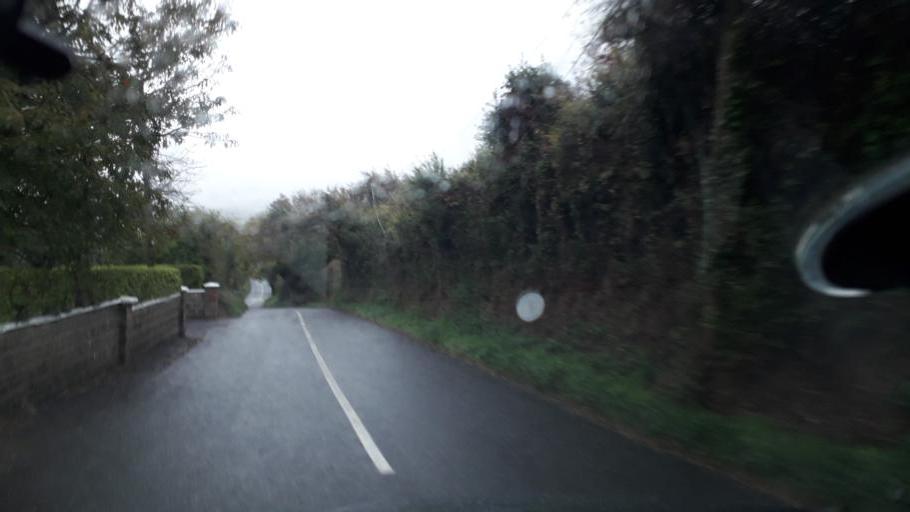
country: IE
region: Leinster
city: Ballyboden
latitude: 53.2619
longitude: -6.3068
